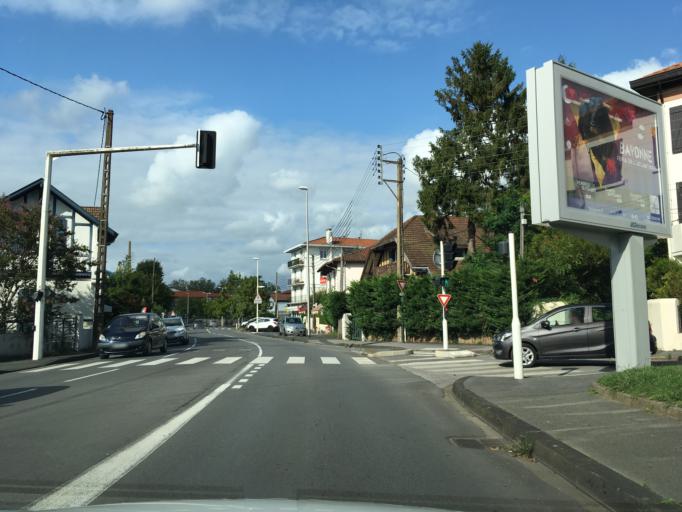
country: FR
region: Aquitaine
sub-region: Departement des Pyrenees-Atlantiques
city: Bayonne
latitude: 43.4754
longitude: -1.4844
